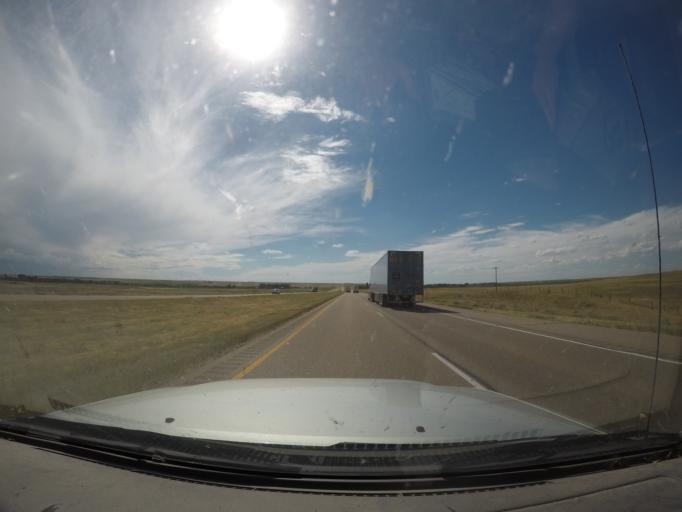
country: US
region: Nebraska
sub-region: Deuel County
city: Chappell
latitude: 41.0535
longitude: -102.4019
